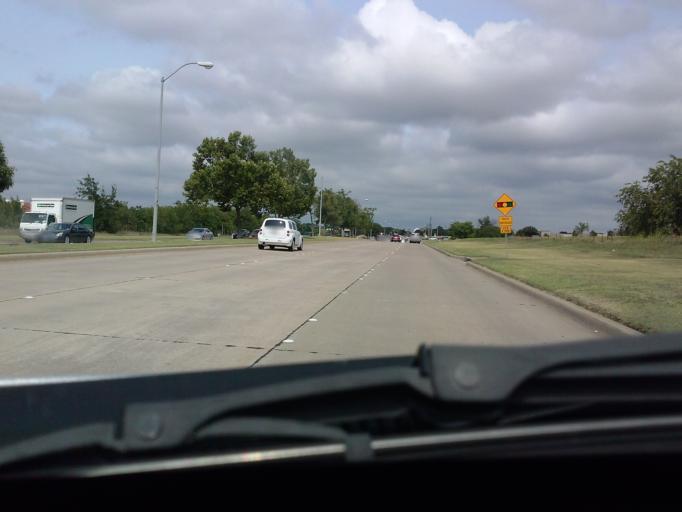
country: US
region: Texas
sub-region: Denton County
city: The Colony
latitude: 33.0565
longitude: -96.7992
